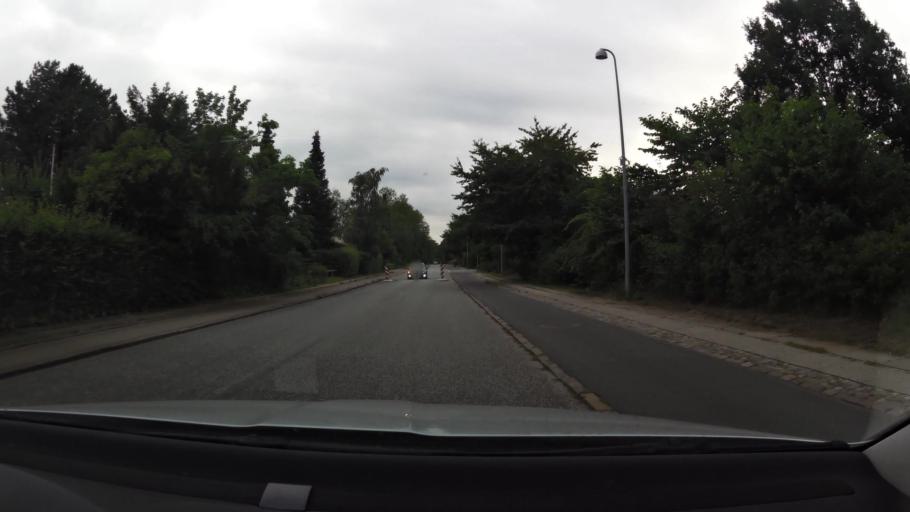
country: DK
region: Capital Region
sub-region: Lyngby-Tarbaek Kommune
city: Kongens Lyngby
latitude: 55.7984
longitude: 12.5120
